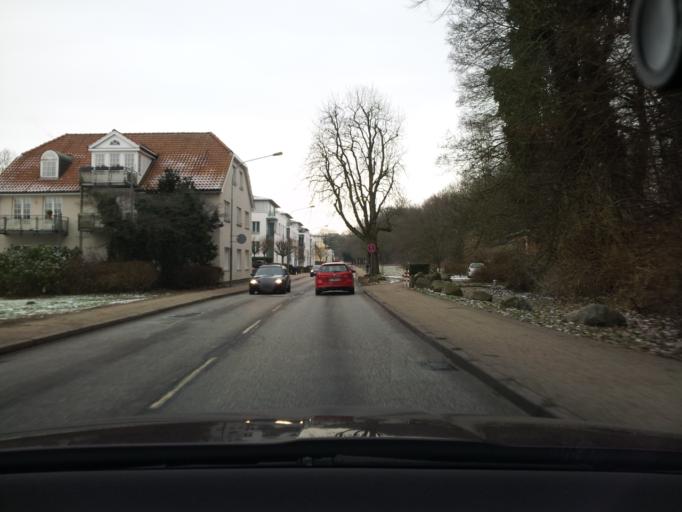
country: DE
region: Schleswig-Holstein
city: Luebeck
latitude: 53.8610
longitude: 10.6805
